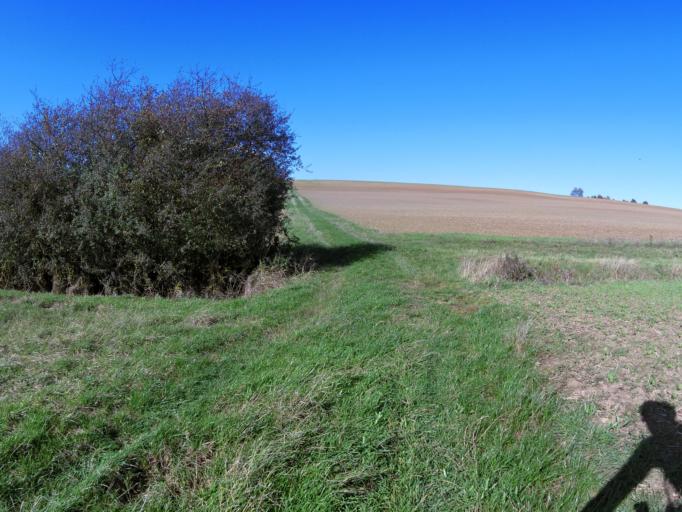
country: DE
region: Bavaria
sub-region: Regierungsbezirk Unterfranken
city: Theilheim
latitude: 49.7658
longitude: 10.0195
